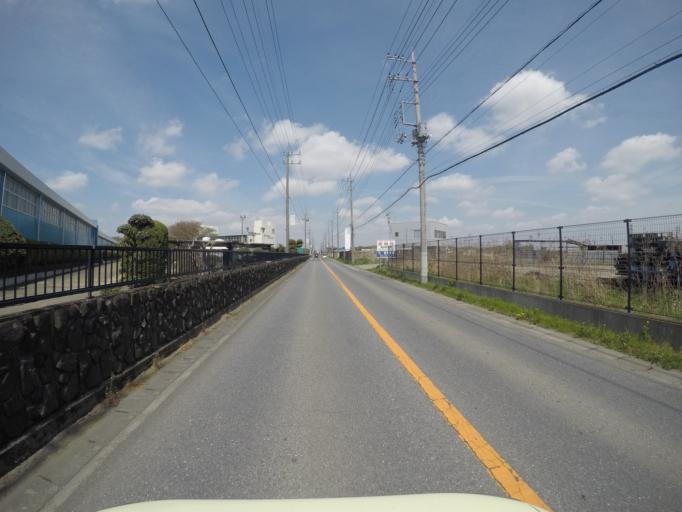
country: JP
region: Ibaraki
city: Tsukuba
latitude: 36.2333
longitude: 140.0557
